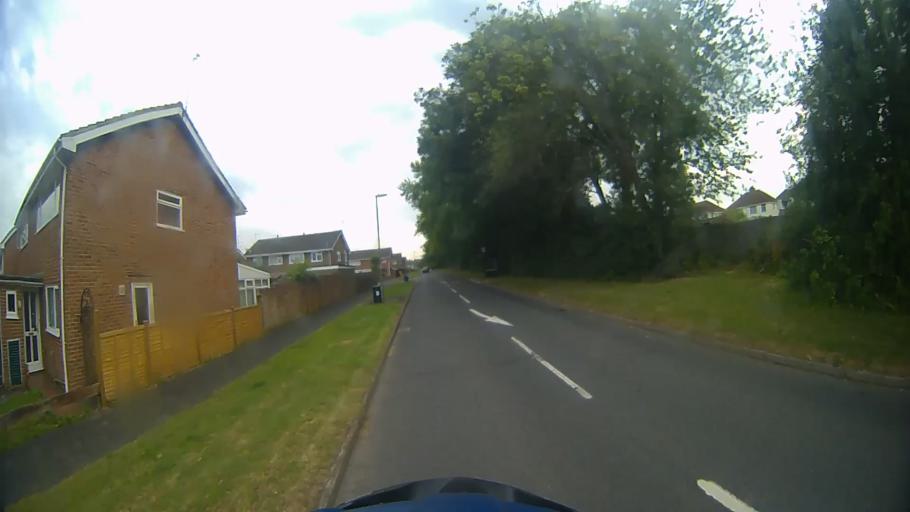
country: GB
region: England
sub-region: Hampshire
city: Basingstoke
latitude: 51.2485
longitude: -1.1088
